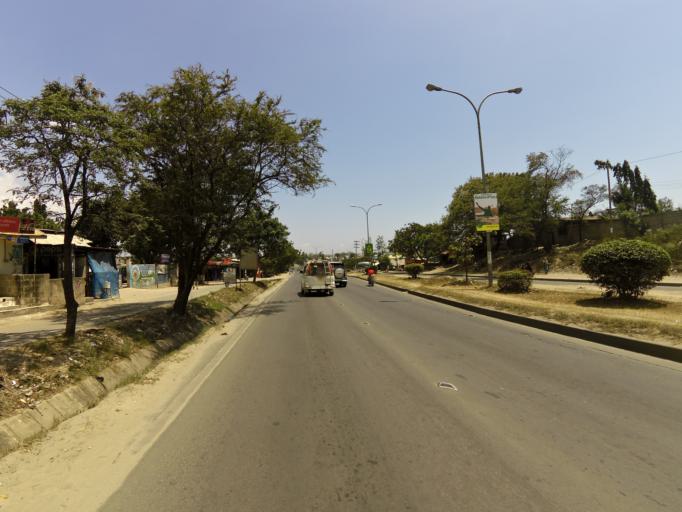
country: TZ
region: Dar es Salaam
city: Dar es Salaam
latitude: -6.8216
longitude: 39.2578
